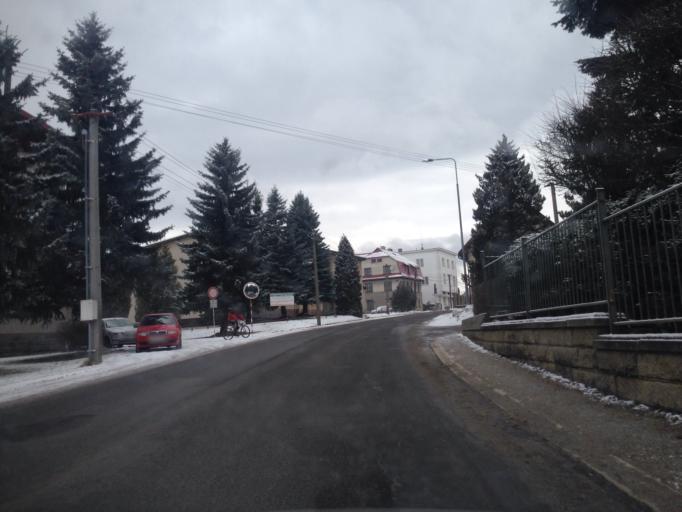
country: CZ
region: Liberecky
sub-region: Okres Semily
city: Vysoke nad Jizerou
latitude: 50.6824
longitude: 15.4035
